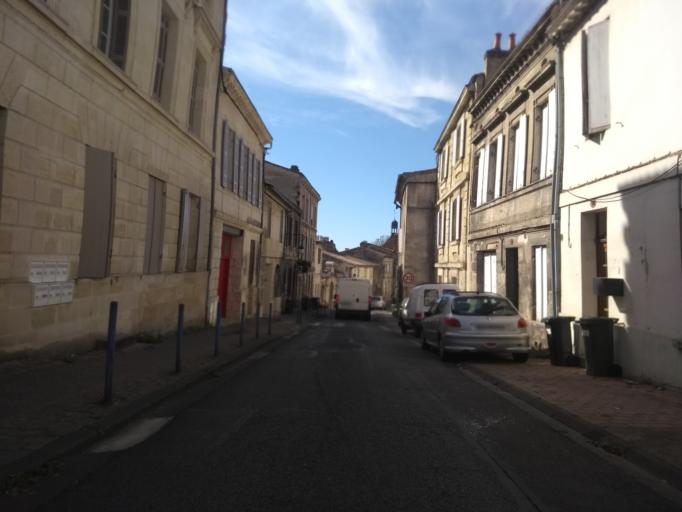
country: FR
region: Aquitaine
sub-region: Departement de la Gironde
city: Lormont
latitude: 44.8775
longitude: -0.5293
